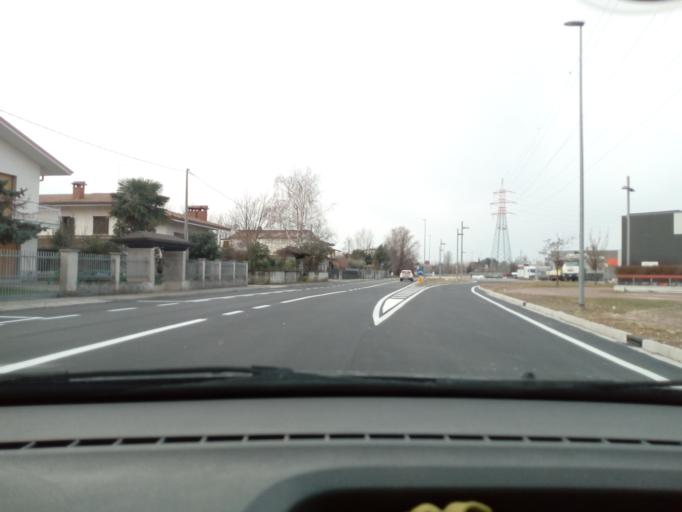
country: IT
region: Friuli Venezia Giulia
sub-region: Provincia di Gorizia
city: Ronchi dei Legionari
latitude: 45.8414
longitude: 13.4915
